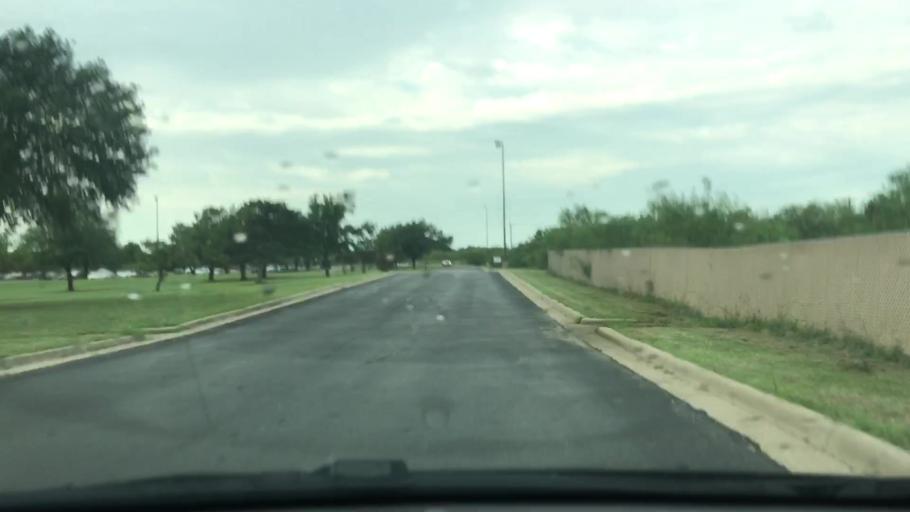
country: US
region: Texas
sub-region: Denton County
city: Denton
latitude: 33.2558
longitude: -97.1505
